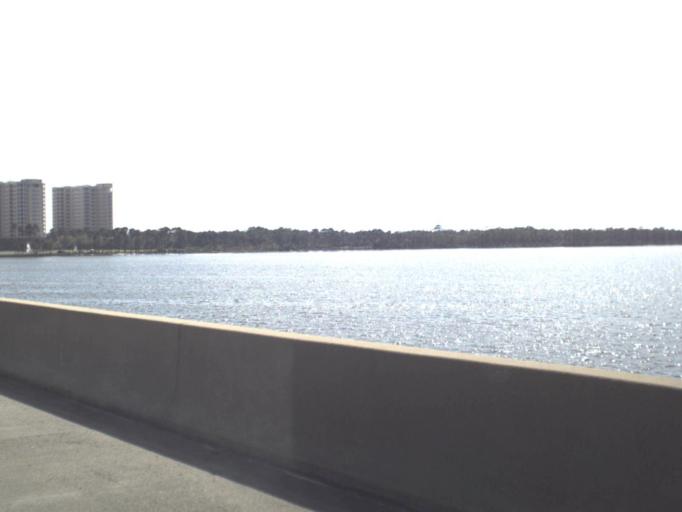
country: US
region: Florida
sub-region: Okaloosa County
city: Destin
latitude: 30.4082
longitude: -86.4239
